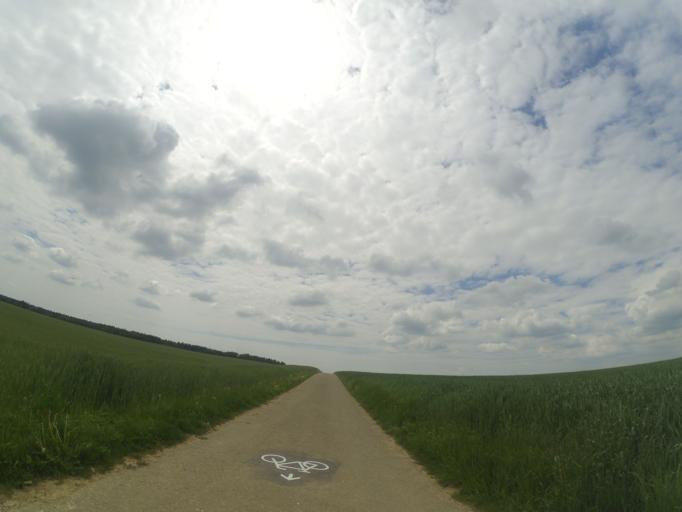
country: DE
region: Baden-Wuerttemberg
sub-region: Tuebingen Region
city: Blaubeuren
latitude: 48.4297
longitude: 9.8293
